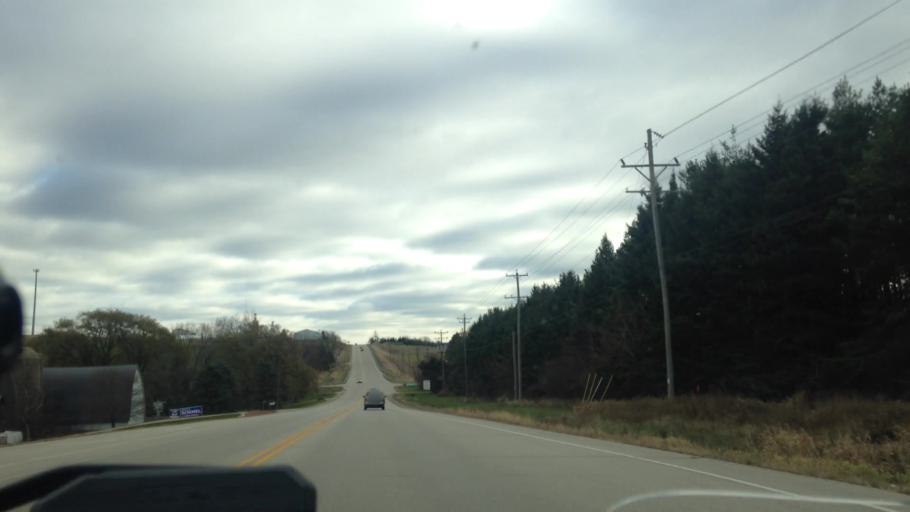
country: US
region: Wisconsin
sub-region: Washington County
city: Slinger
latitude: 43.4275
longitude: -88.2958
